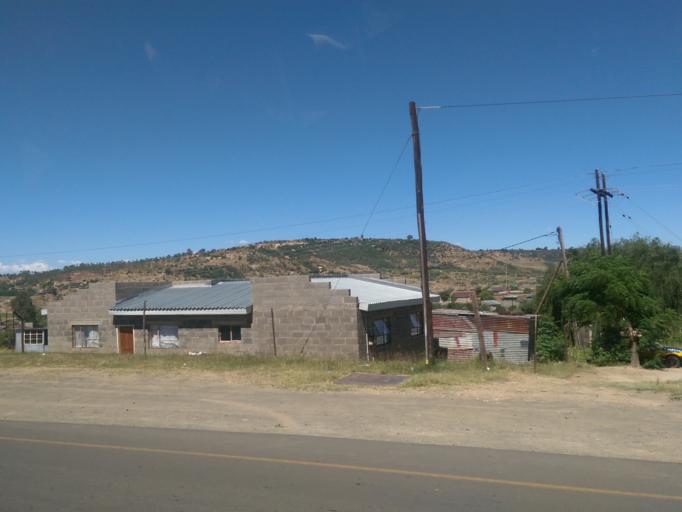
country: LS
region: Maseru
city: Maseru
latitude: -29.4084
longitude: 27.5611
